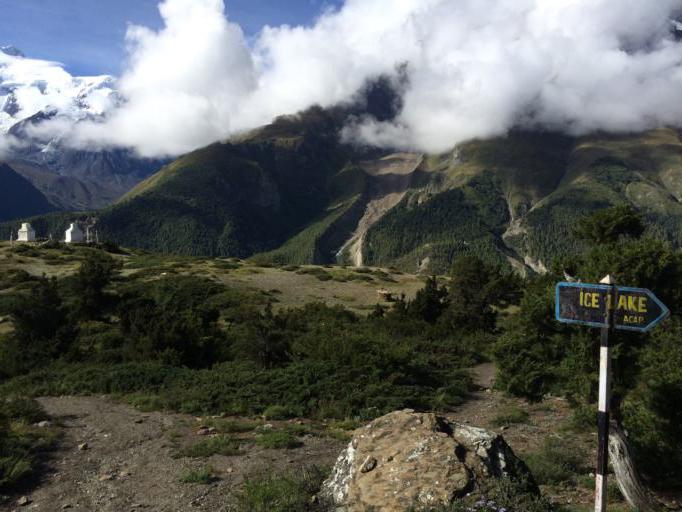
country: NP
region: Western Region
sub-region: Gandaki Zone
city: Nawal
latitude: 28.6598
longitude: 84.0508
